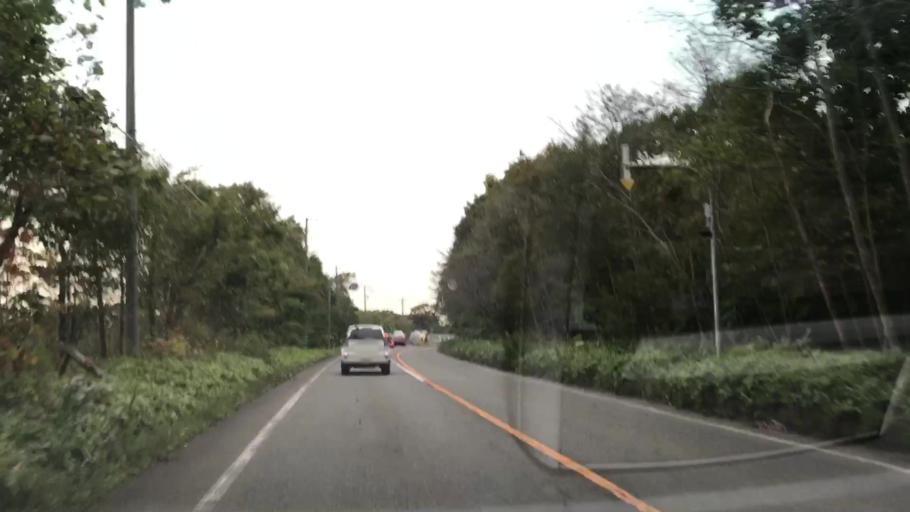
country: JP
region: Hokkaido
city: Tomakomai
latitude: 42.7060
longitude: 141.6634
